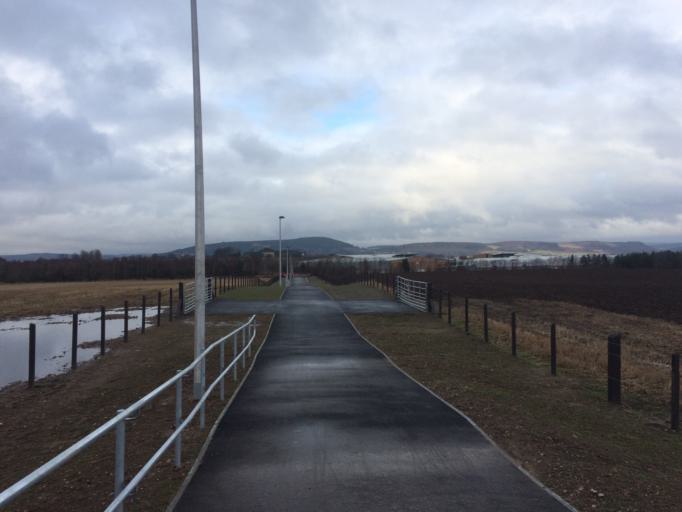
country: GB
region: Scotland
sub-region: Highland
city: Inverness
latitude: 57.4774
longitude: -4.1750
